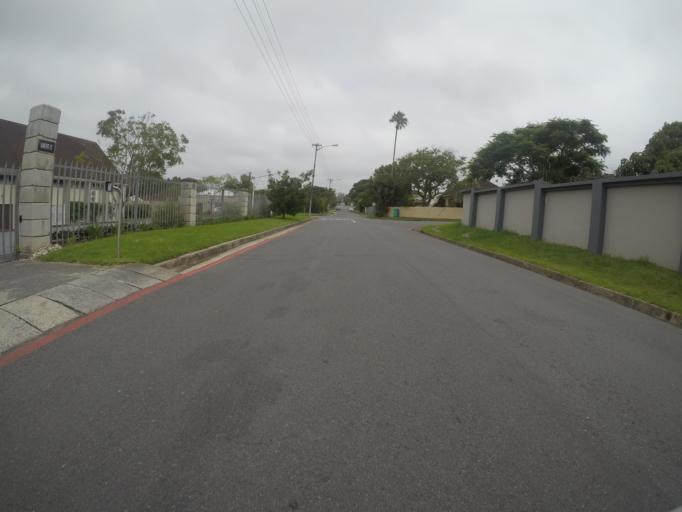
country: ZA
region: Eastern Cape
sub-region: Buffalo City Metropolitan Municipality
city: East London
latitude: -32.9877
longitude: 27.9275
